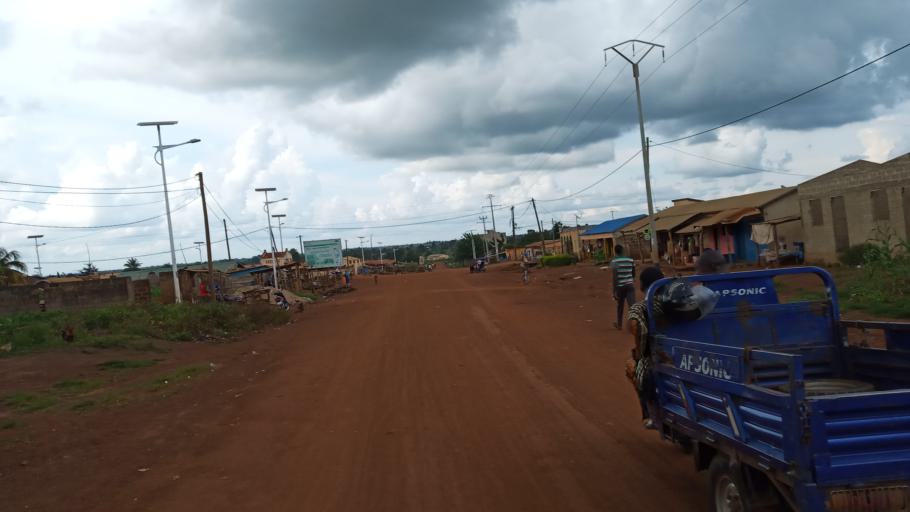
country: TG
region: Centrale
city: Sotouboua
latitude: 8.5572
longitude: 0.9848
